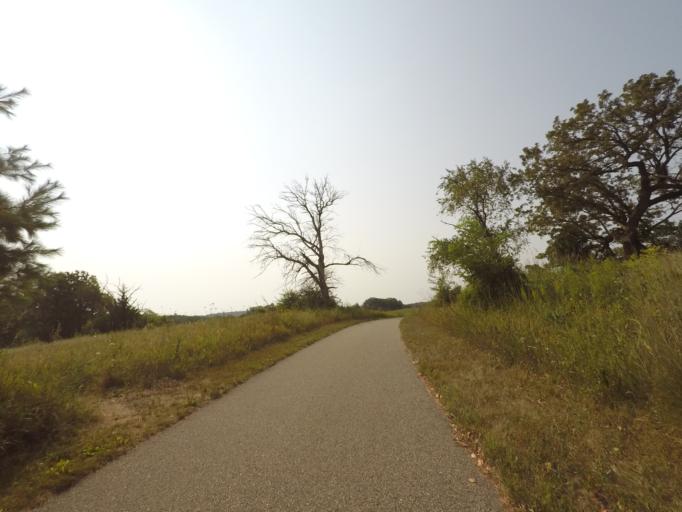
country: US
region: Wisconsin
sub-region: Waukesha County
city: Delafield
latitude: 43.0475
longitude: -88.4134
